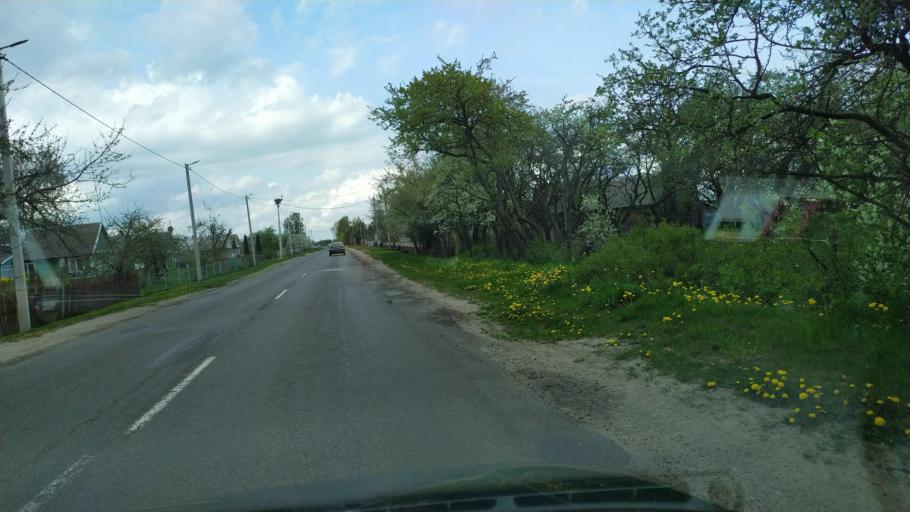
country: BY
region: Brest
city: Pruzhany
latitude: 52.5901
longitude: 24.4091
